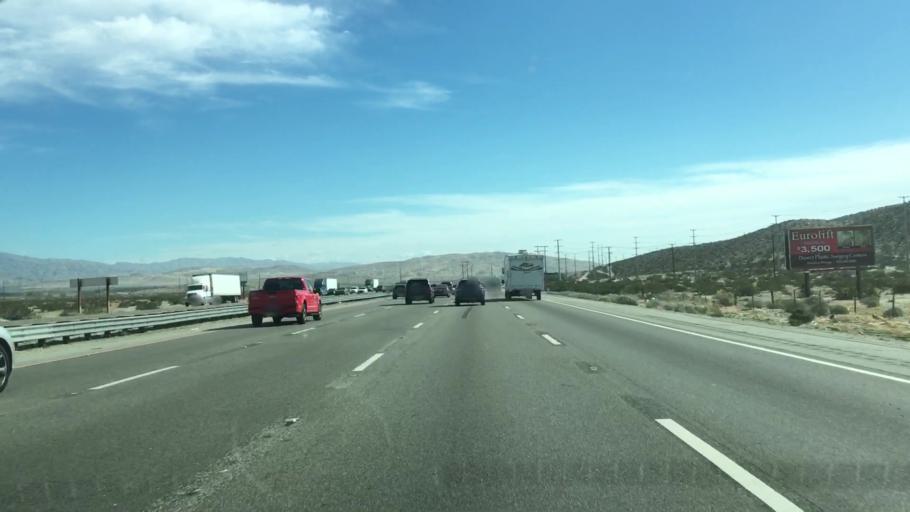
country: US
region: California
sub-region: Riverside County
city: Garnet
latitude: 33.9019
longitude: -116.5360
